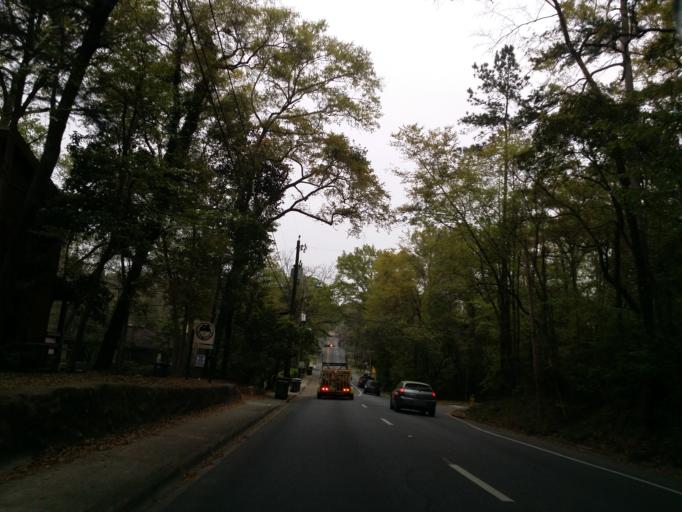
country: US
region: Florida
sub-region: Leon County
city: Tallahassee
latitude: 30.4521
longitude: -84.2831
